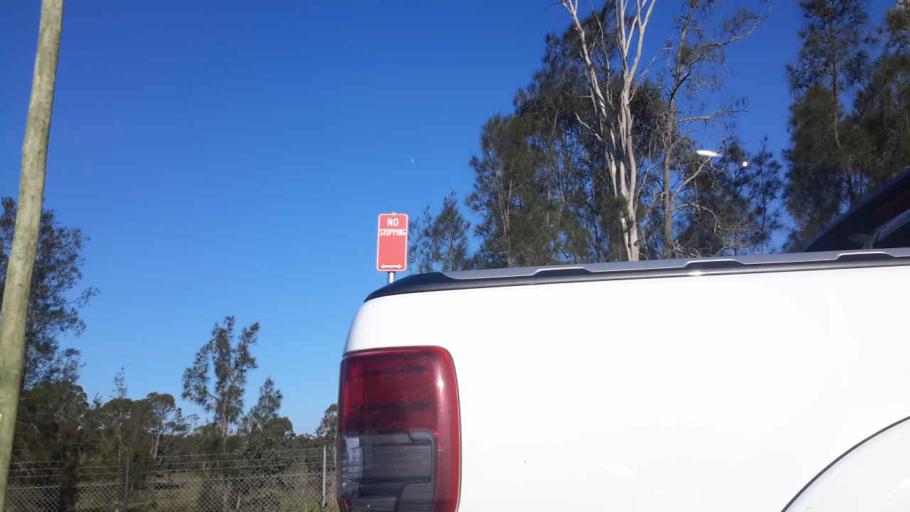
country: AU
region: New South Wales
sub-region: Penrith Municipality
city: Glenmore Park
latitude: -33.8050
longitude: 150.6963
